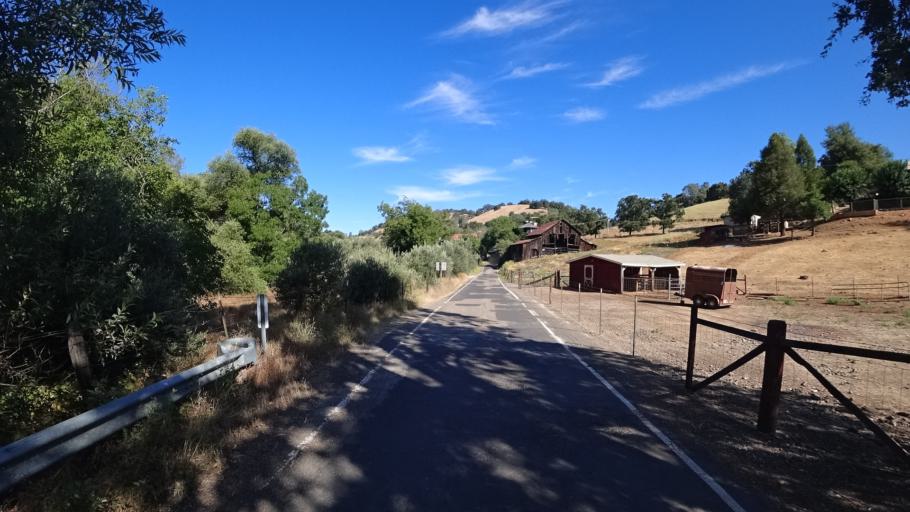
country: US
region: California
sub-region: Calaveras County
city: San Andreas
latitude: 38.1565
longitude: -120.6103
